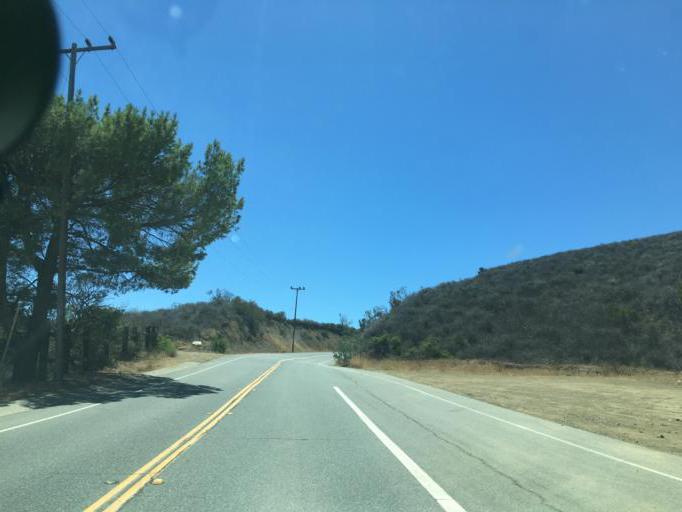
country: US
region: California
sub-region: Los Angeles County
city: Malibu
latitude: 34.0627
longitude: -118.8741
